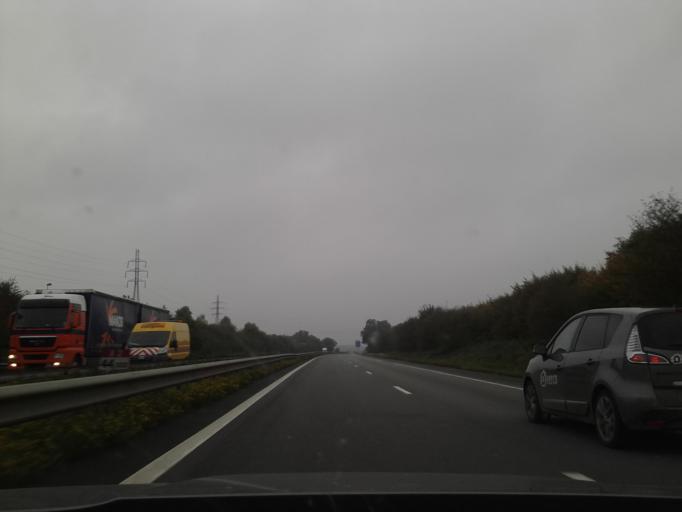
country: FR
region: Nord-Pas-de-Calais
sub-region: Departement du Nord
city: Hordain
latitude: 50.2620
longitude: 3.3295
